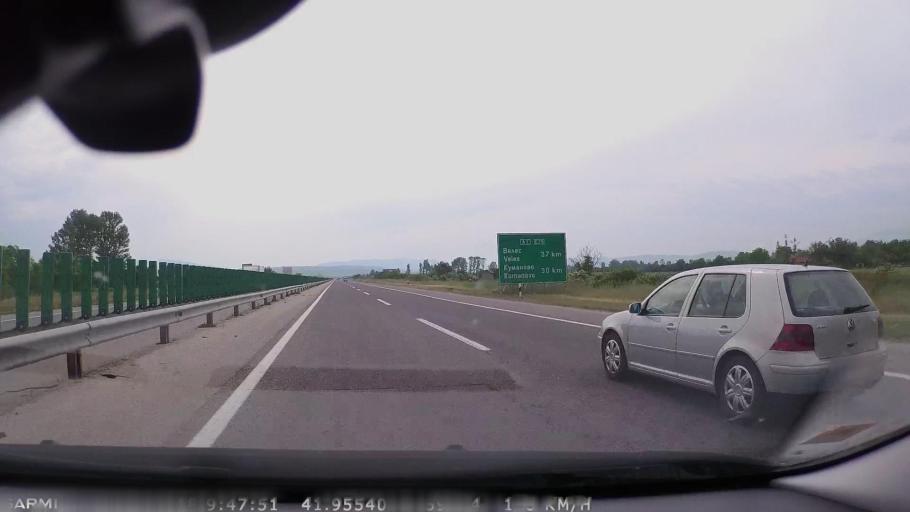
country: MK
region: Ilinden
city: Idrizovo
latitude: 41.9672
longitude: 21.5739
